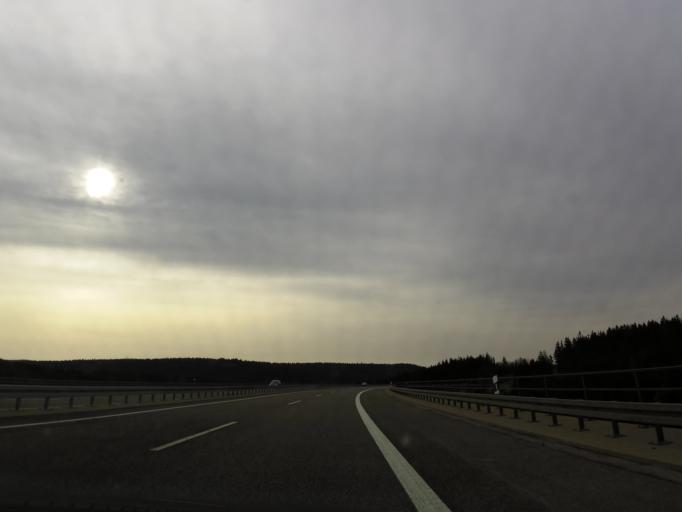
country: DE
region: Thuringia
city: Suhl
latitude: 50.5742
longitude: 10.7263
